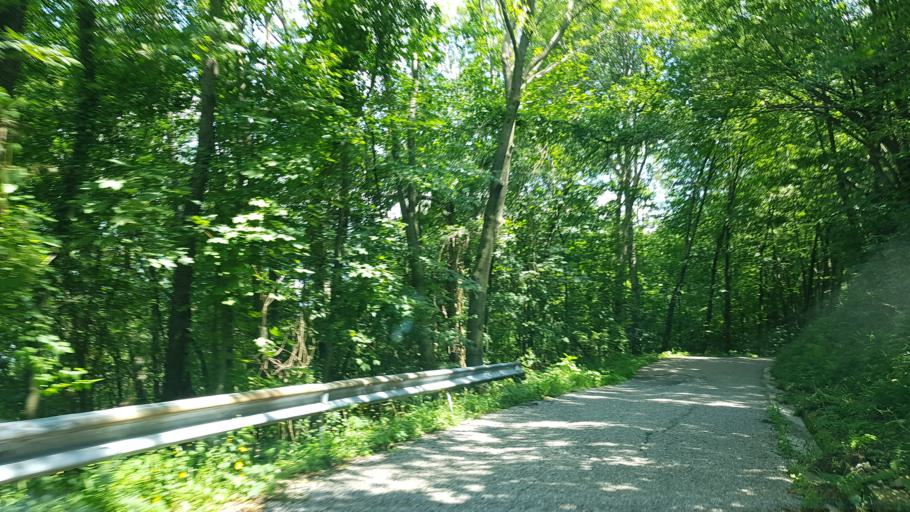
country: IT
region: Friuli Venezia Giulia
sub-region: Provincia di Udine
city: Lusevera
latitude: 46.2474
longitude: 13.2725
